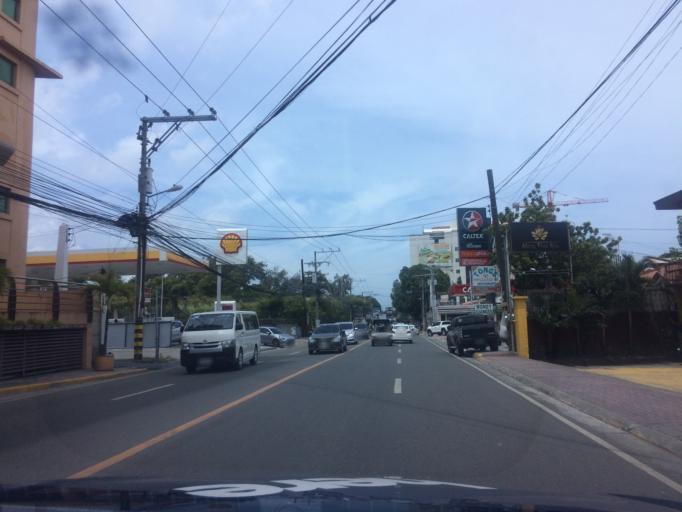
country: PH
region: Central Visayas
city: Mandaue City
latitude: 10.3245
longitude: 123.9155
